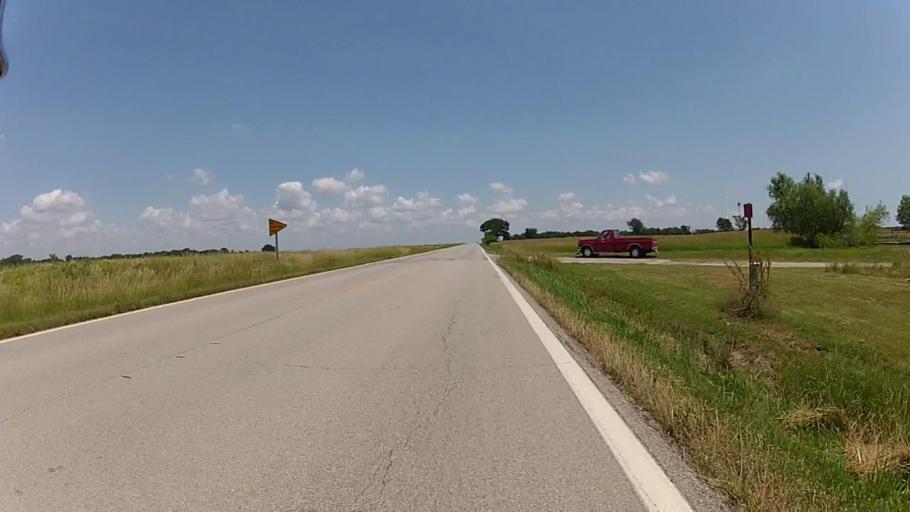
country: US
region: Kansas
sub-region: Montgomery County
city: Cherryvale
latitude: 37.1927
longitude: -95.4468
